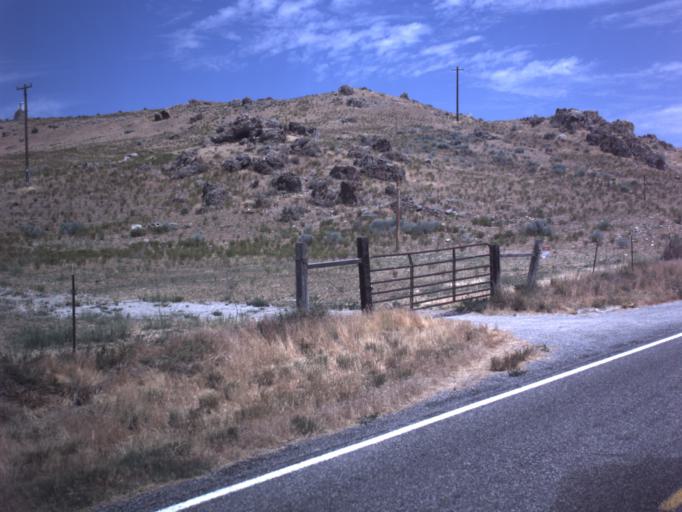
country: US
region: Utah
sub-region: Box Elder County
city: Tremonton
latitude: 41.6223
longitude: -112.3511
